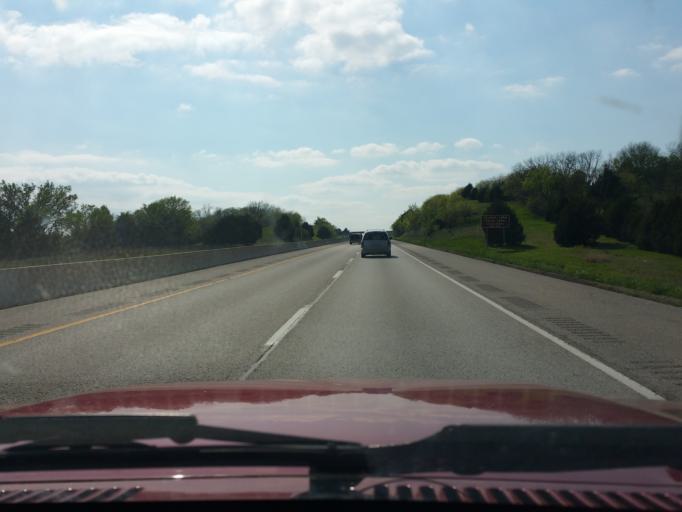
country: US
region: Kansas
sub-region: Douglas County
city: Lawrence
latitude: 38.9979
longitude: -95.3075
